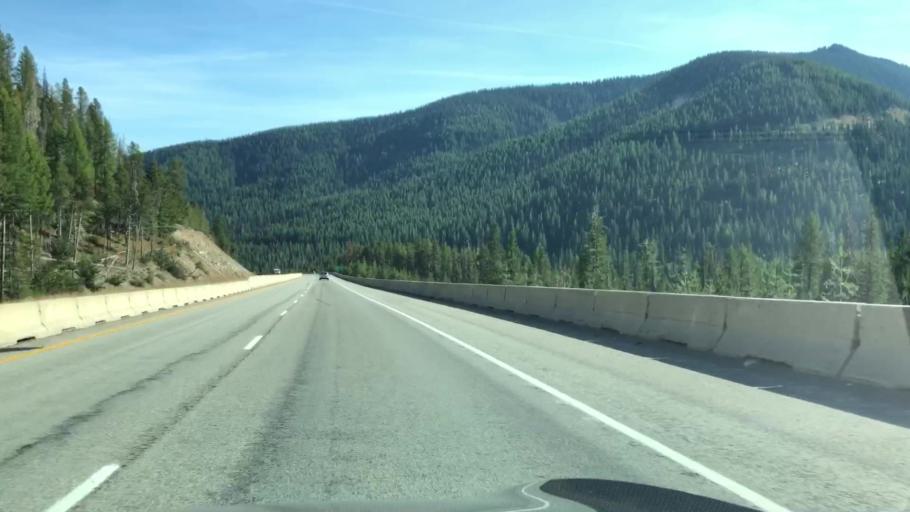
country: US
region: Idaho
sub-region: Shoshone County
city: Wallace
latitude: 47.4465
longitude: -115.6930
